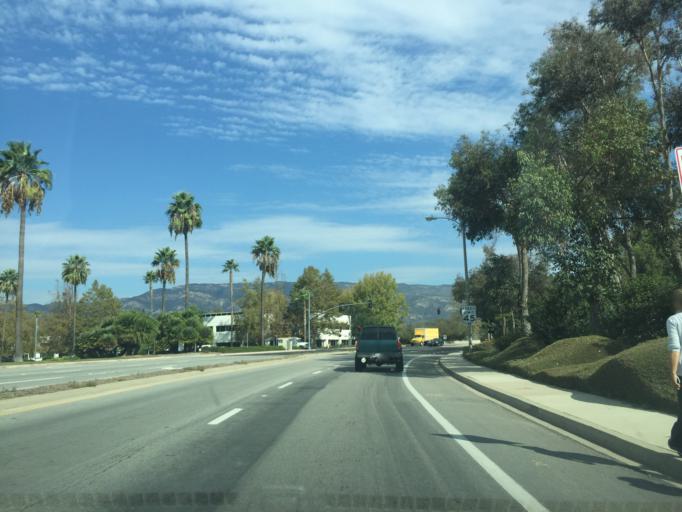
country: US
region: California
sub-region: Santa Barbara County
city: Isla Vista
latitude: 34.4308
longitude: -119.8596
